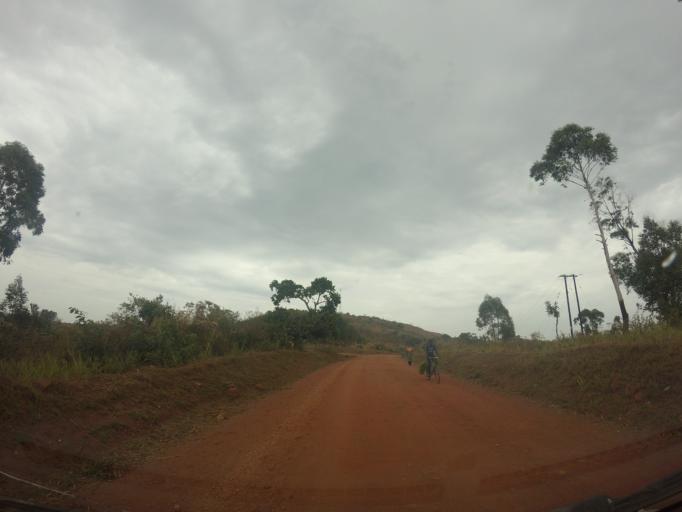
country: UG
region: Northern Region
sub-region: Zombo District
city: Zombo
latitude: 2.7625
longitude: 30.8537
